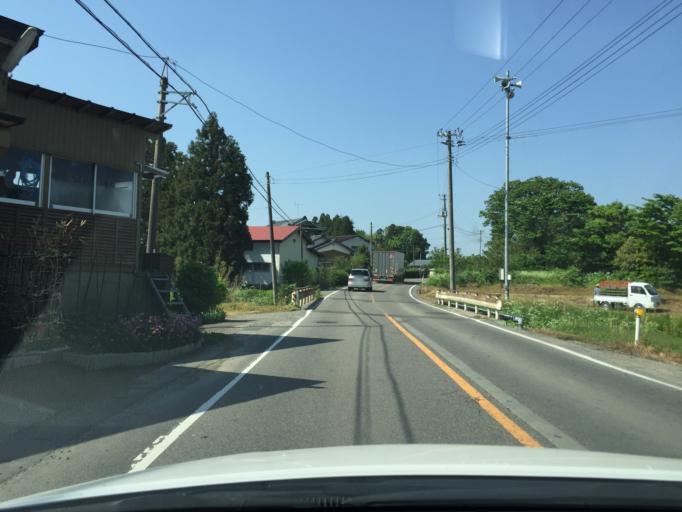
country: JP
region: Niigata
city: Muramatsu
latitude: 37.7098
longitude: 139.2057
